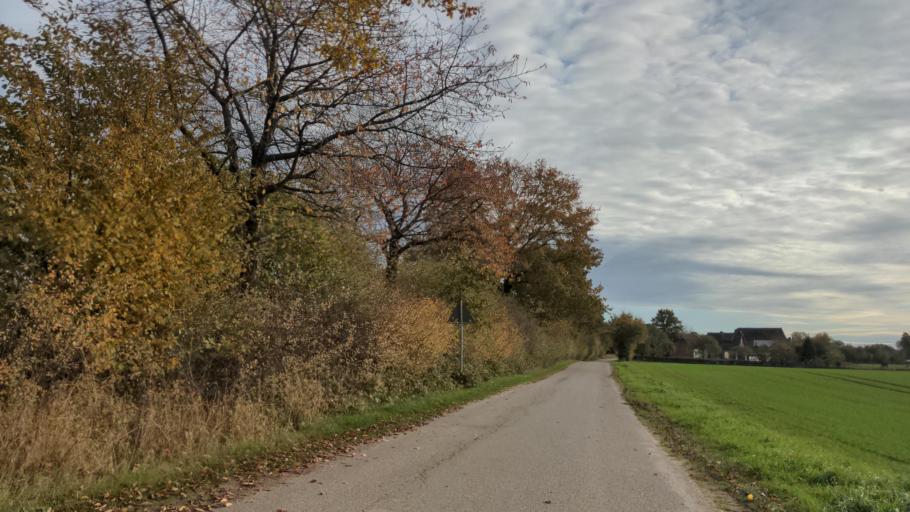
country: DE
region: Schleswig-Holstein
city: Bosdorf
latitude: 54.1170
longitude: 10.4990
